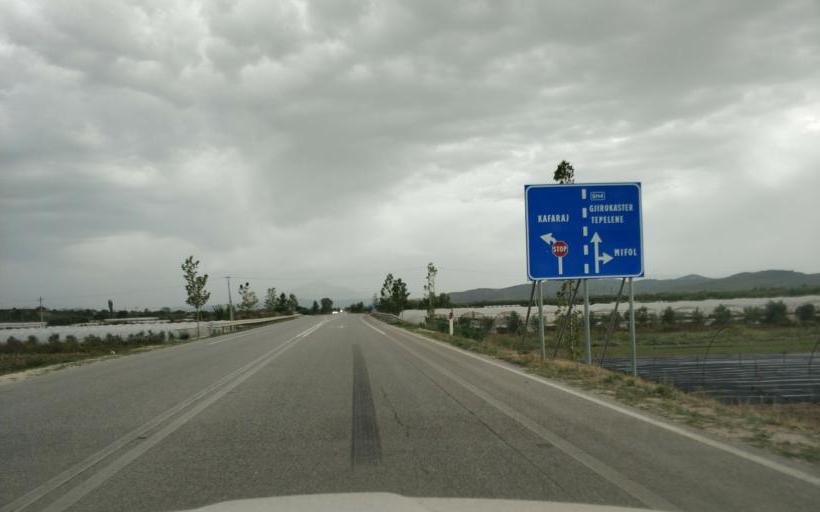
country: AL
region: Fier
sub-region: Rrethi i Fierit
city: Frakulla e Madhe
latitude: 40.6323
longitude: 19.5076
